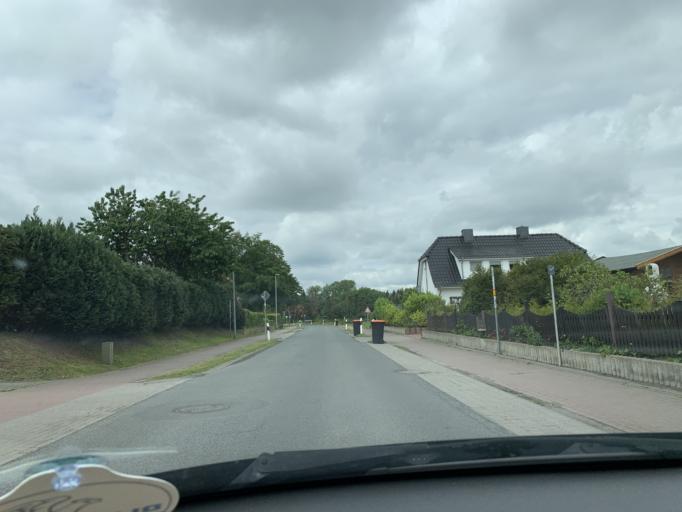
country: DE
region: Lower Saxony
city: Varel
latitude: 53.3769
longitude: 8.0927
